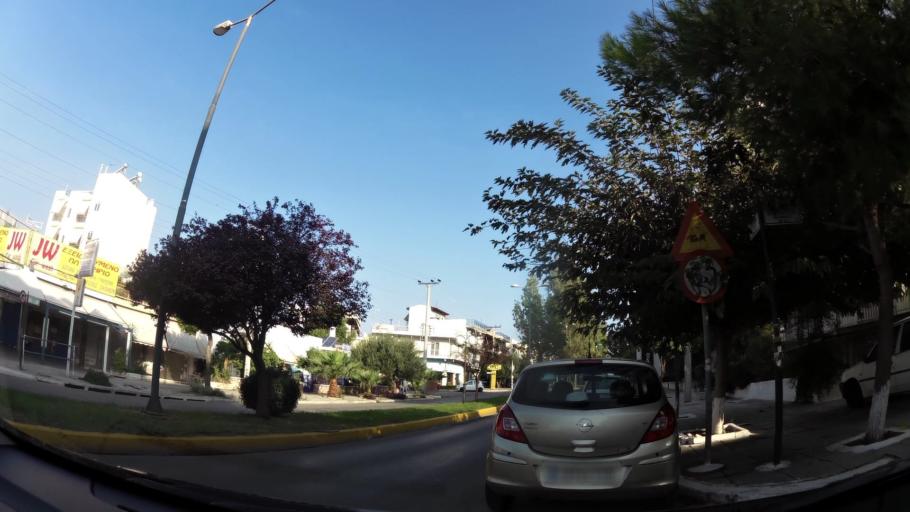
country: GR
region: Attica
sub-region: Nomarchia Athinas
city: Ilioupoli
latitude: 37.9313
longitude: 23.7515
